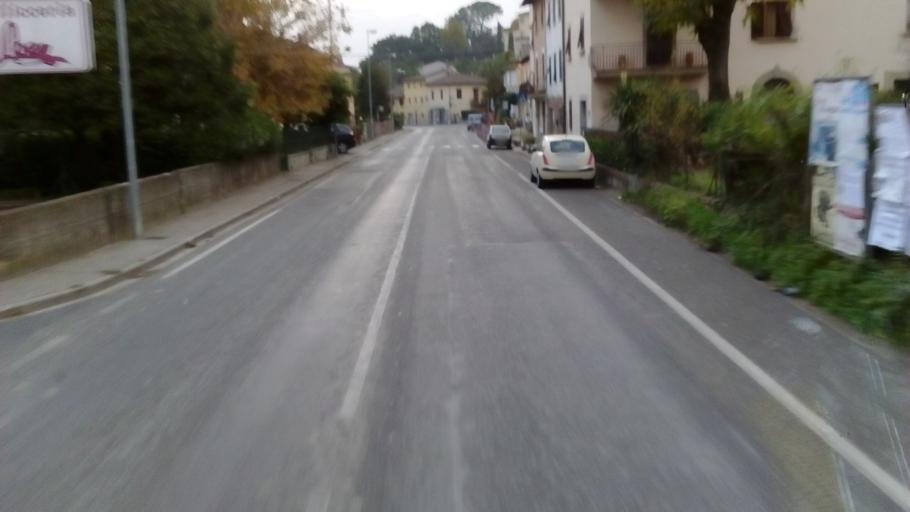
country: IT
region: Tuscany
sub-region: Province of Florence
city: Castelfiorentino
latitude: 43.6317
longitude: 10.9607
